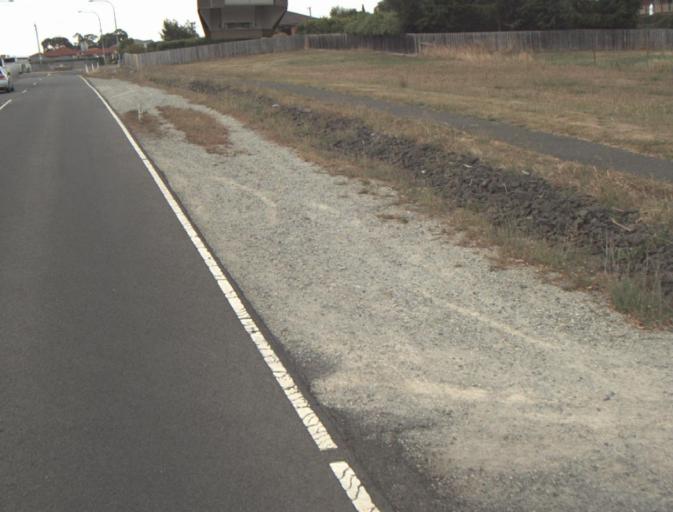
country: AU
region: Tasmania
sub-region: Launceston
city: Newstead
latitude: -41.4764
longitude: 147.1817
